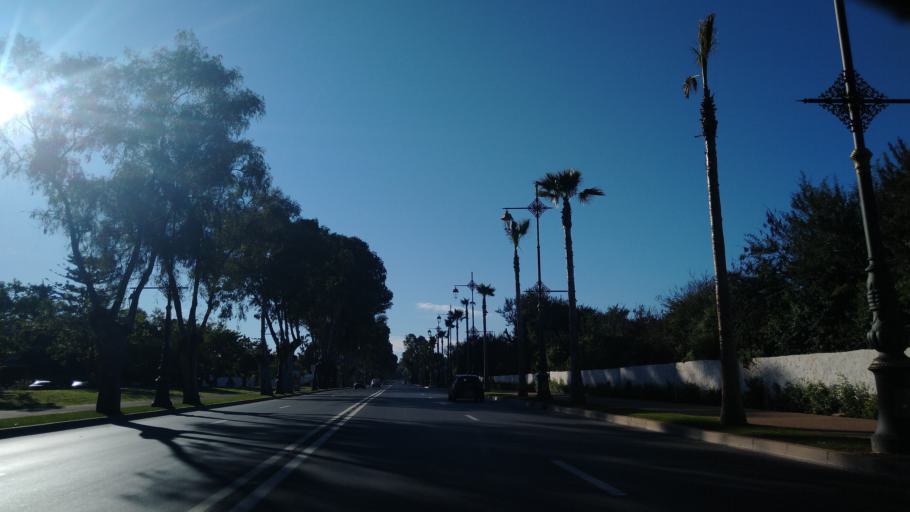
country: MA
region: Rabat-Sale-Zemmour-Zaer
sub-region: Rabat
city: Rabat
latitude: 33.9447
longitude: -6.8222
